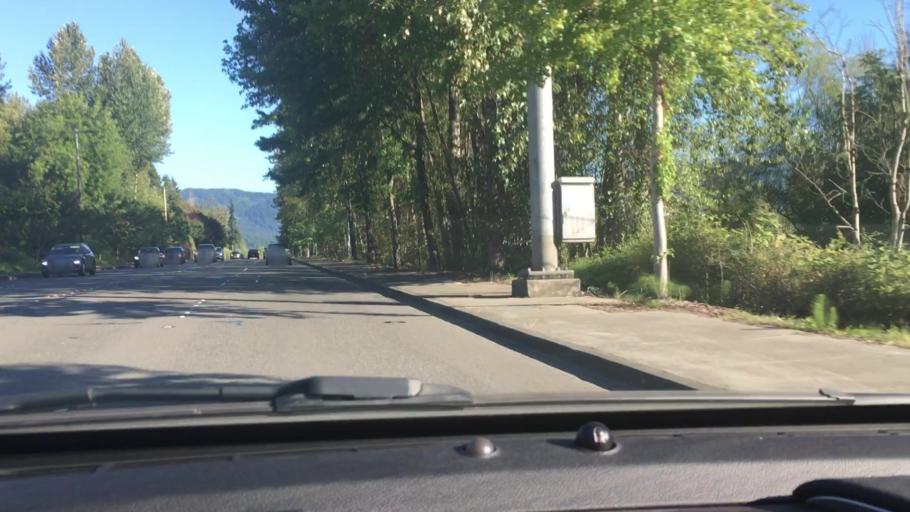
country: US
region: Washington
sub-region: King County
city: Issaquah
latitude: 47.5613
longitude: -122.0497
